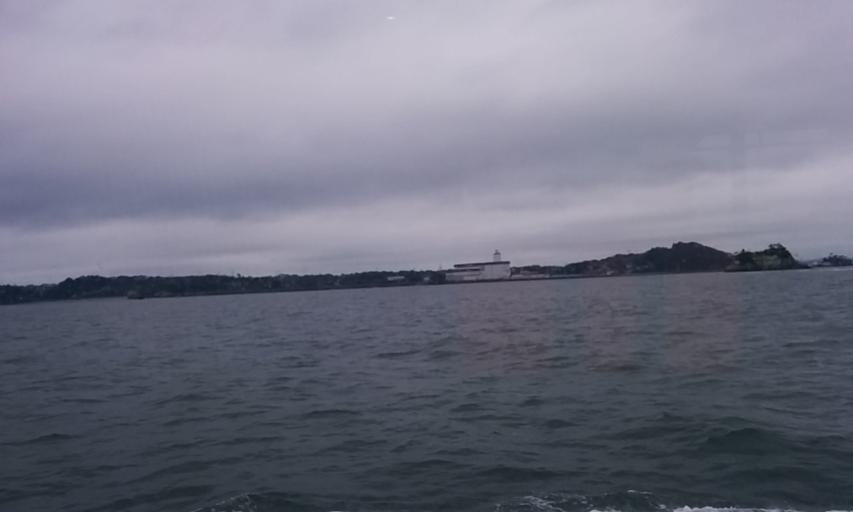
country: JP
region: Miyagi
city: Shiogama
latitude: 38.3249
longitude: 141.0876
